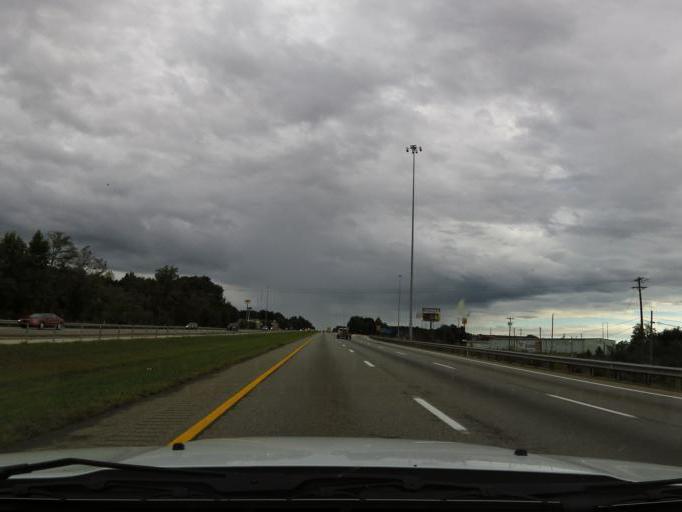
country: US
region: Kentucky
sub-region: Laurel County
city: North Corbin
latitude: 36.9721
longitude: -84.1116
